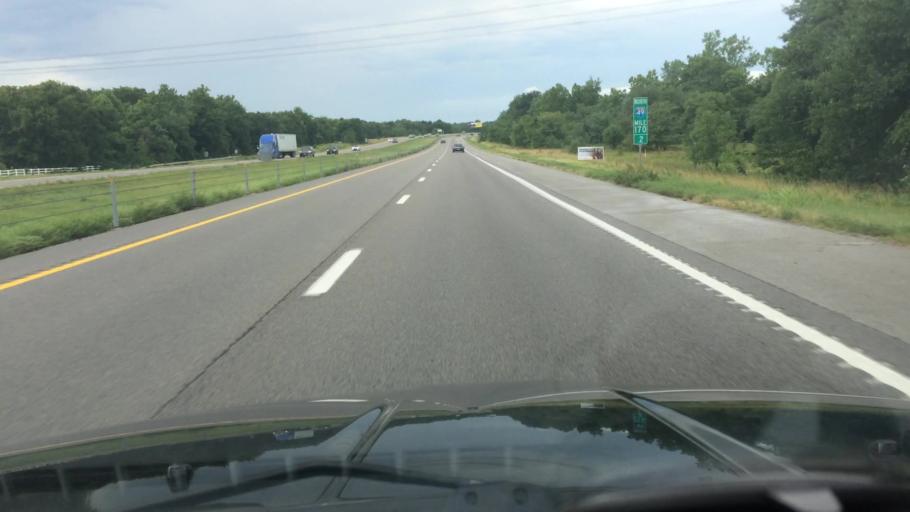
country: US
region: Missouri
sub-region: Cass County
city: Peculiar
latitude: 38.7585
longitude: -94.4841
